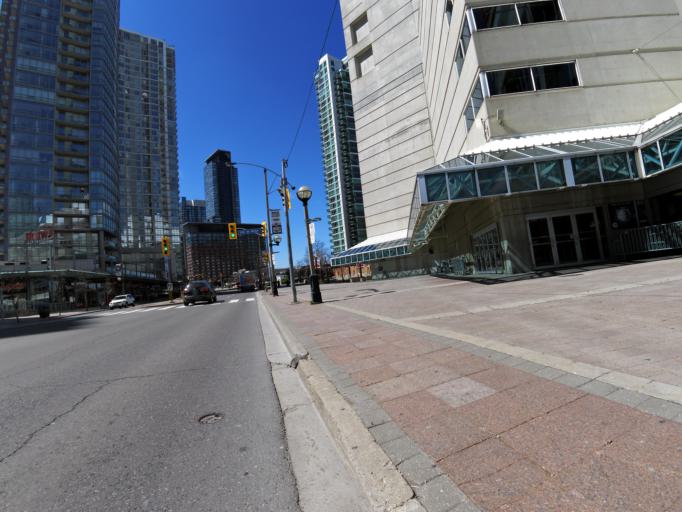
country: CA
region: Ontario
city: Toronto
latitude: 43.6406
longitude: -79.3898
